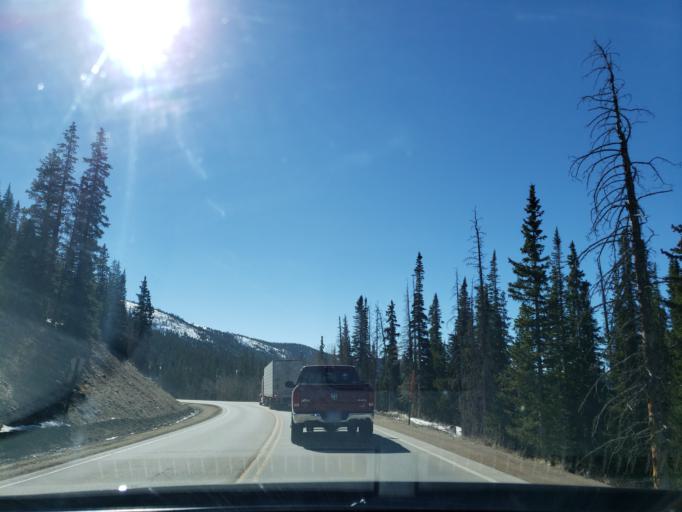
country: US
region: Colorado
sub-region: Park County
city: Fairplay
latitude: 39.3479
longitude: -106.0548
